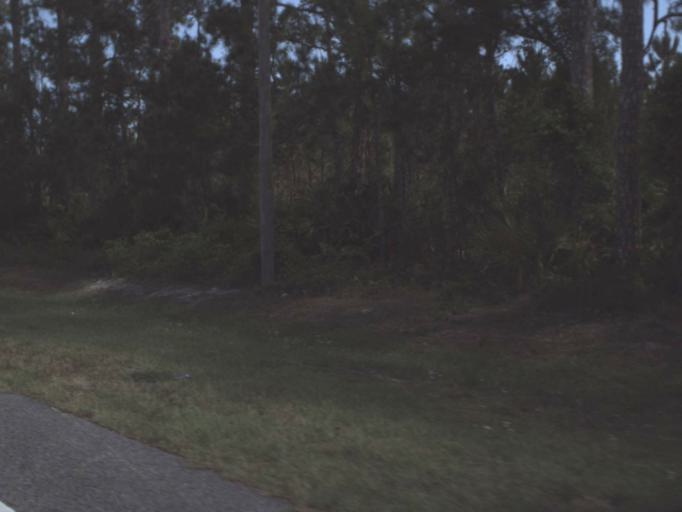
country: US
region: Florida
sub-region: Flagler County
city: Bunnell
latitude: 29.3862
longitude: -81.1888
